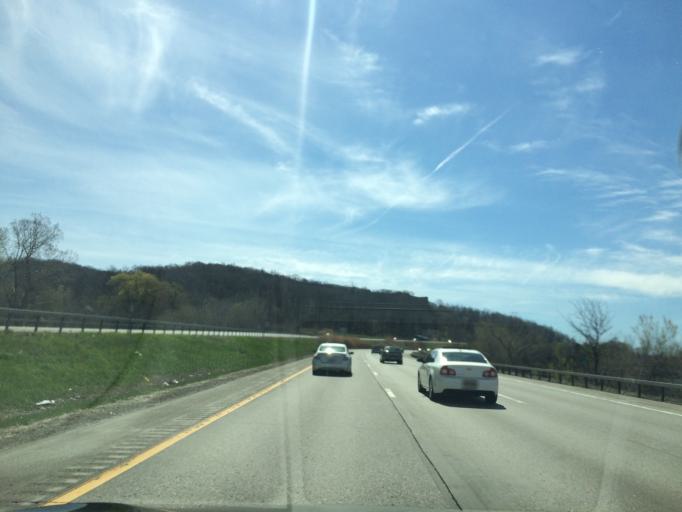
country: US
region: New York
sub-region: Monroe County
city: Fairport
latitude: 43.0512
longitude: -77.4676
